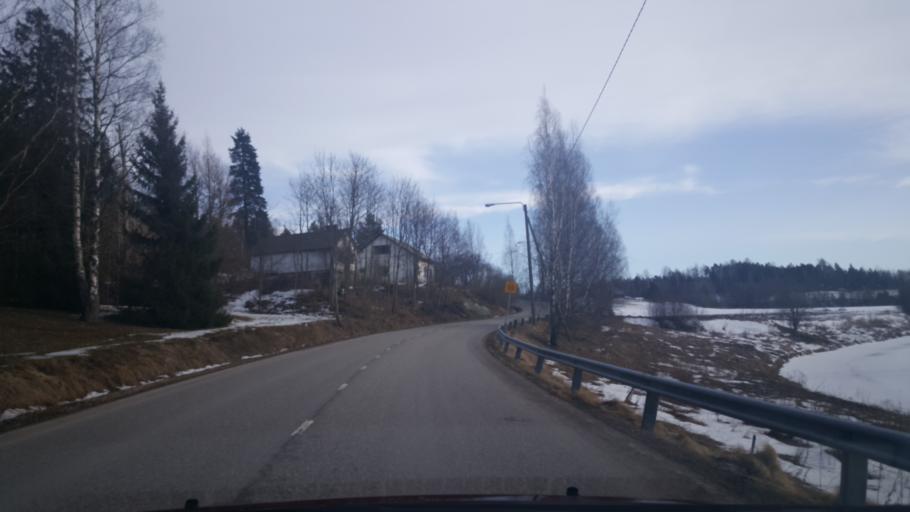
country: FI
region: Uusimaa
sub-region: Helsinki
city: Teekkarikylae
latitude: 60.2917
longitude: 24.8879
